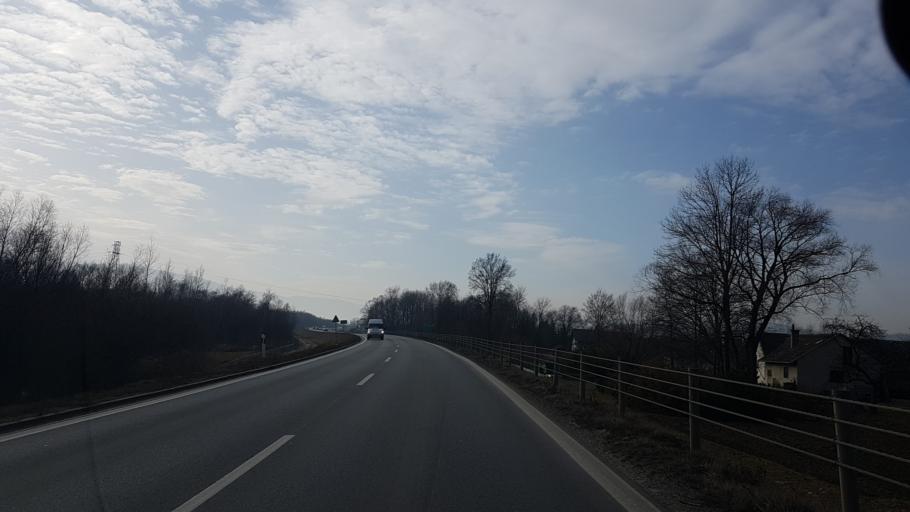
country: PL
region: Lesser Poland Voivodeship
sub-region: Powiat nowosadecki
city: Podegrodzie
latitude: 49.5779
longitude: 20.6112
